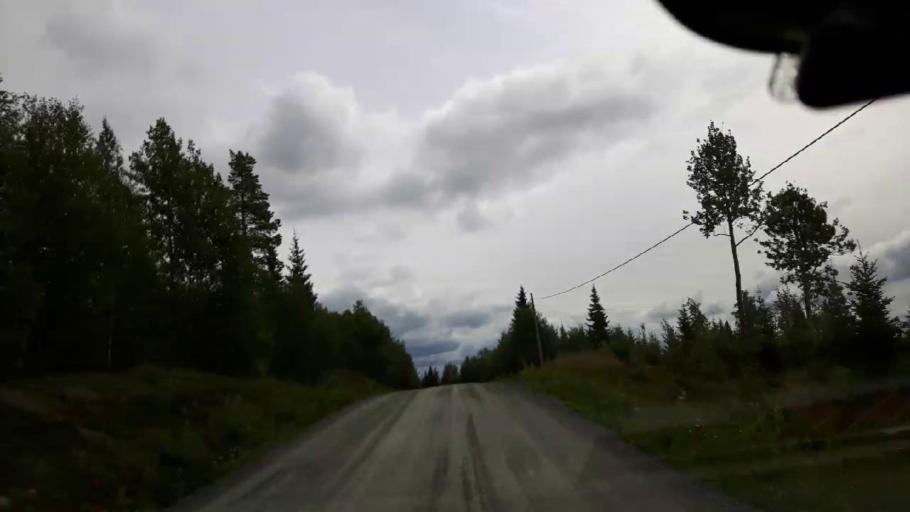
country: SE
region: Jaemtland
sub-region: Krokoms Kommun
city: Valla
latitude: 63.6845
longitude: 13.9169
